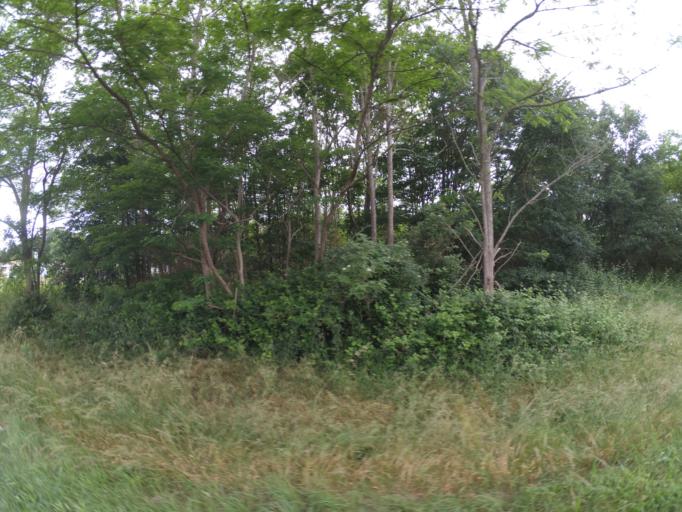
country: FR
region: Aquitaine
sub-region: Departement de la Gironde
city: Lamarque
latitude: 45.0858
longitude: -0.7270
